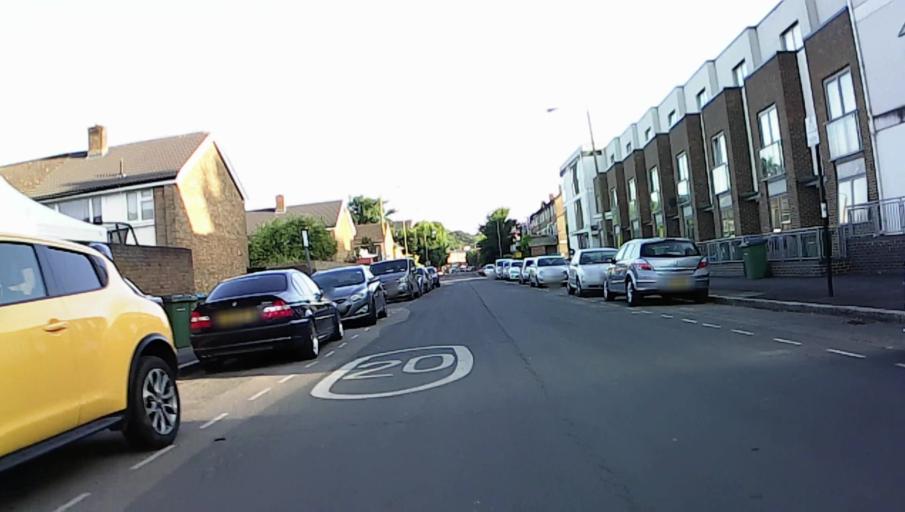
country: GB
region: England
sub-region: Greater London
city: Blackheath
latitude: 51.4882
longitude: 0.0044
